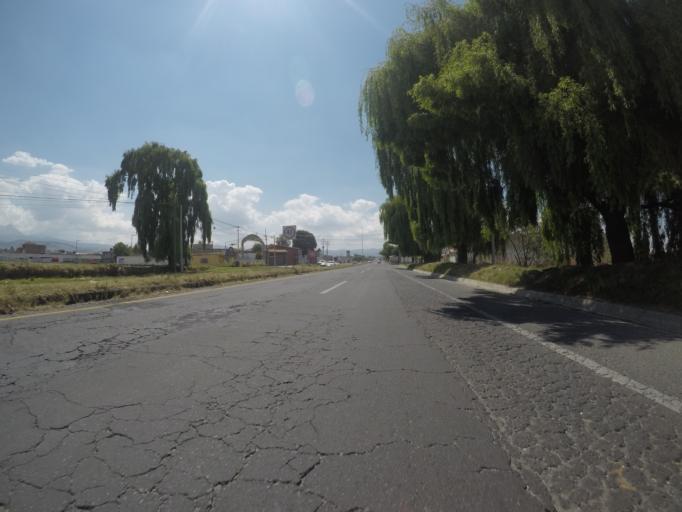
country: MX
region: Mexico
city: Santa Cruz Cuauhtenco
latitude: 19.2546
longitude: -99.7254
